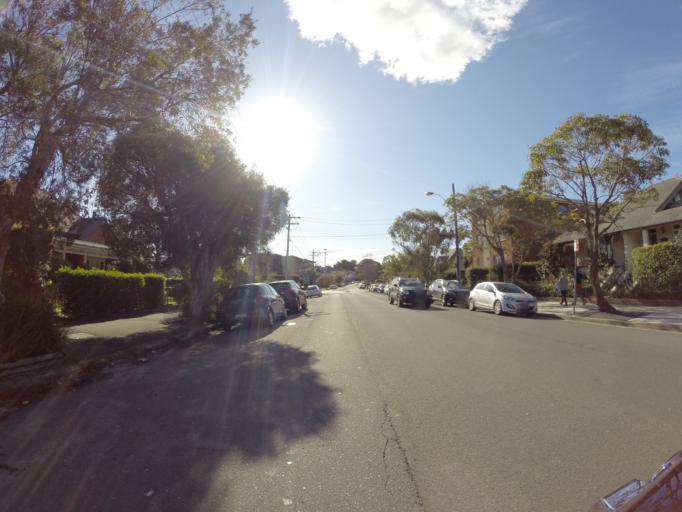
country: AU
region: New South Wales
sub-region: Randwick
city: Randwick
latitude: -33.9225
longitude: 151.2436
